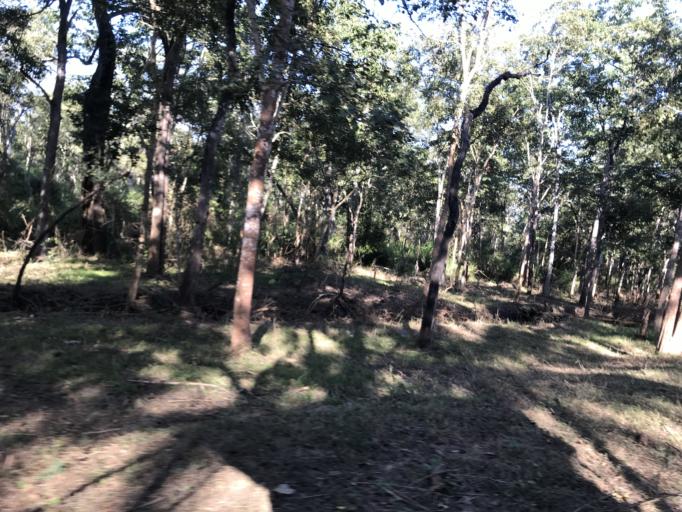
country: IN
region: Karnataka
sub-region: Mysore
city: Heggadadevankote
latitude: 11.9792
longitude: 76.2348
